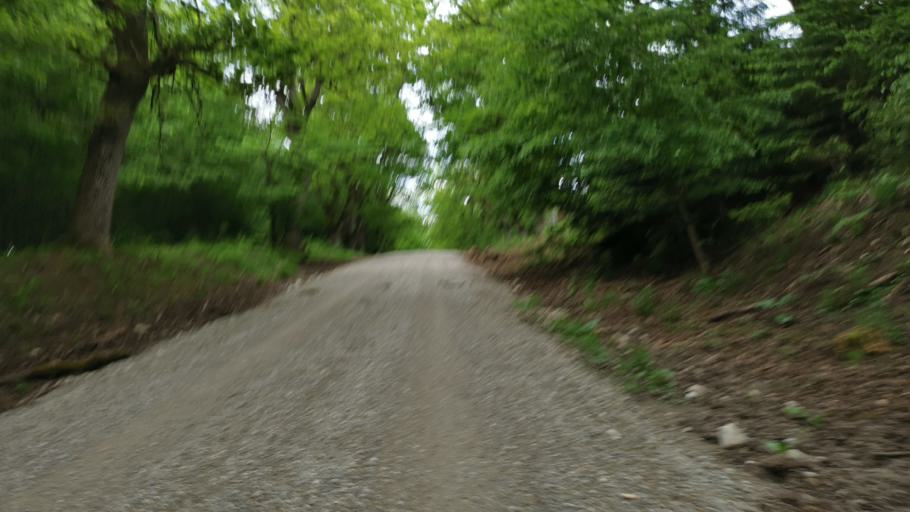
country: DE
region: Bavaria
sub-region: Upper Bavaria
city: Baierbrunn
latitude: 48.0444
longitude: 11.4711
